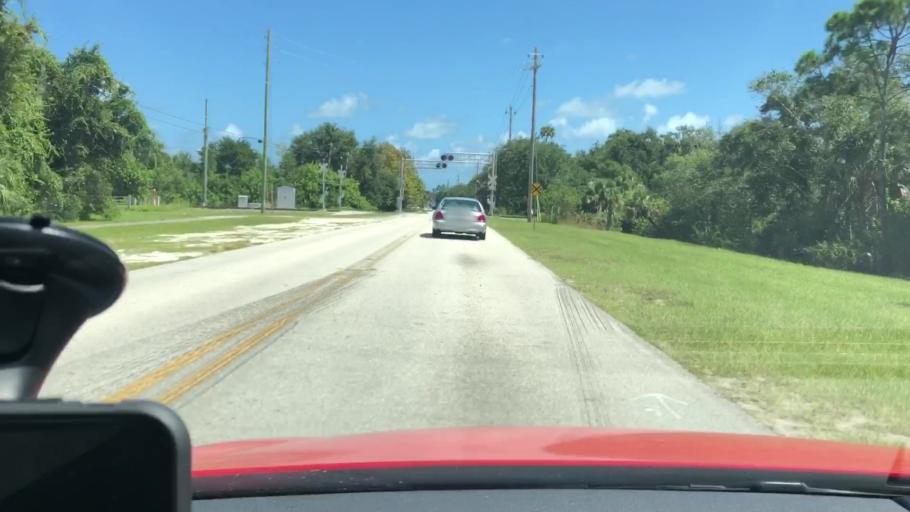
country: US
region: Florida
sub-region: Volusia County
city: Edgewater
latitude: 29.0035
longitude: -80.9190
